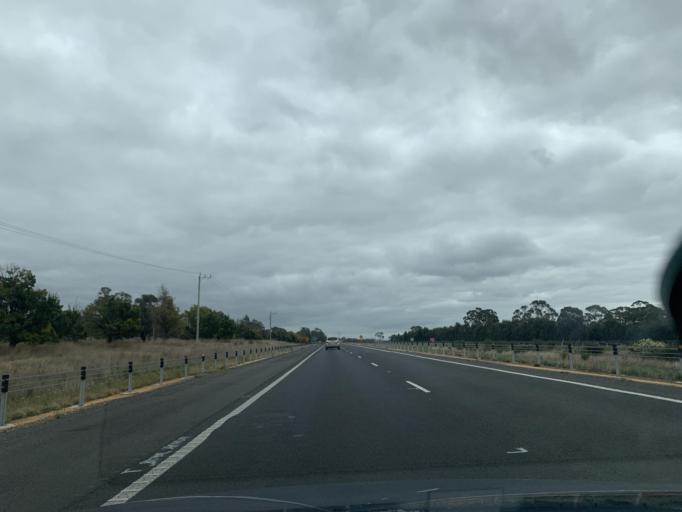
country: AU
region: Victoria
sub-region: Ballarat North
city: Newington
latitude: -37.4347
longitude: 143.4528
